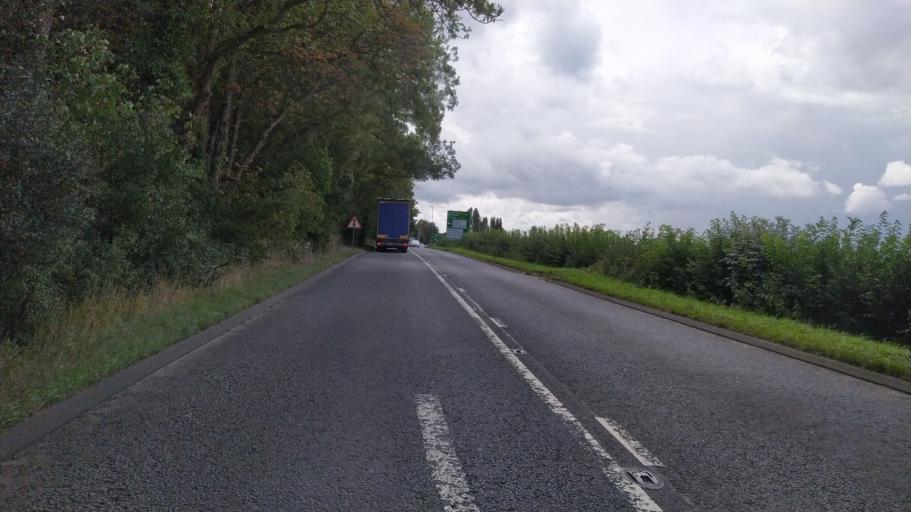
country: GB
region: England
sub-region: Wiltshire
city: North Bradley
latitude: 51.3034
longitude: -2.1756
